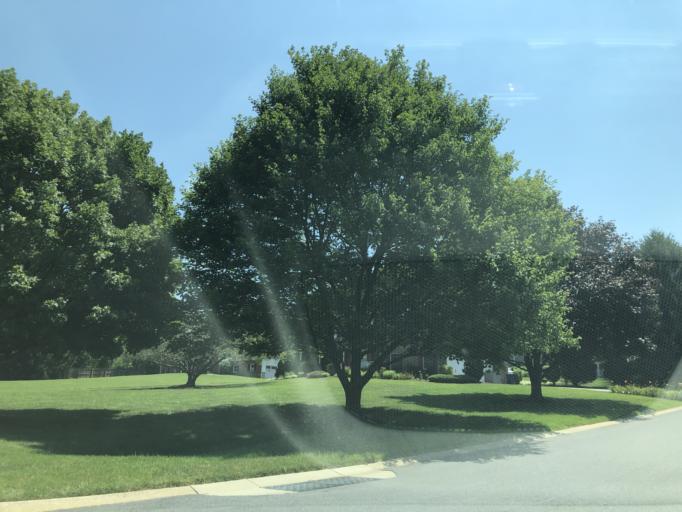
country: US
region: Maryland
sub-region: Carroll County
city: Westminster
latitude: 39.5407
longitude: -76.9871
